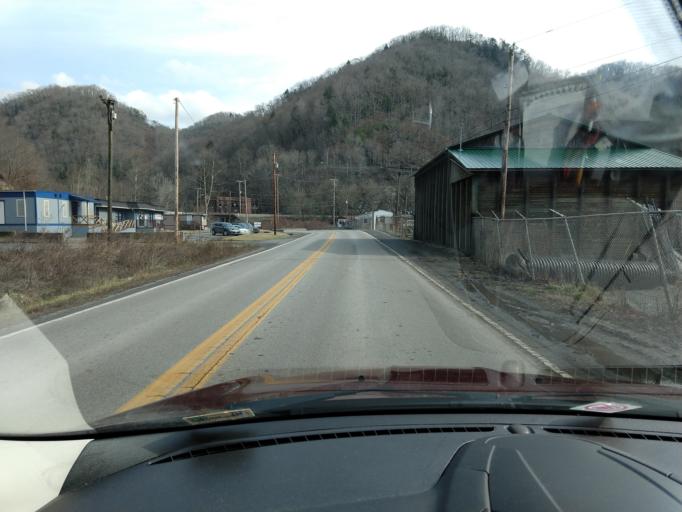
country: US
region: West Virginia
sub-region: McDowell County
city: Welch
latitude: 37.3212
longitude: -81.6976
